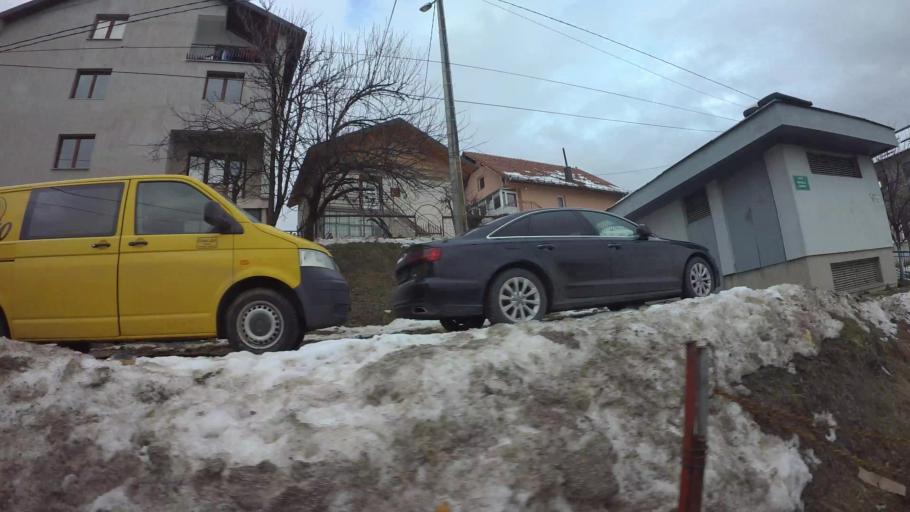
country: BA
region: Federation of Bosnia and Herzegovina
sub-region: Kanton Sarajevo
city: Sarajevo
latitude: 43.8573
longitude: 18.3578
